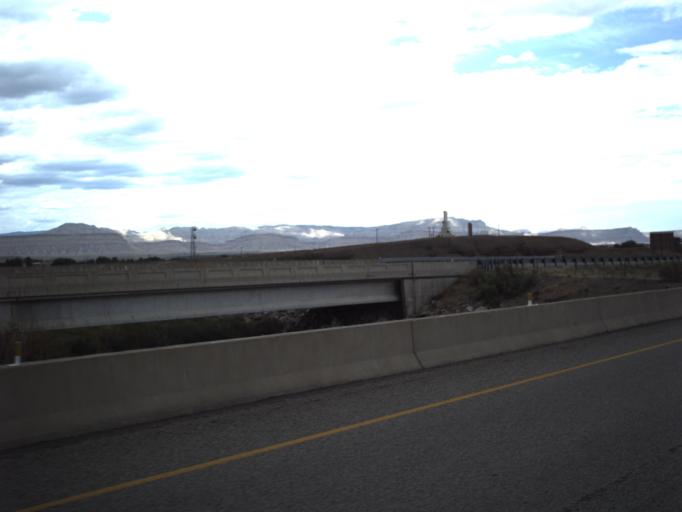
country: US
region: Utah
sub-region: Carbon County
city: East Carbon City
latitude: 38.9905
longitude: -110.1748
